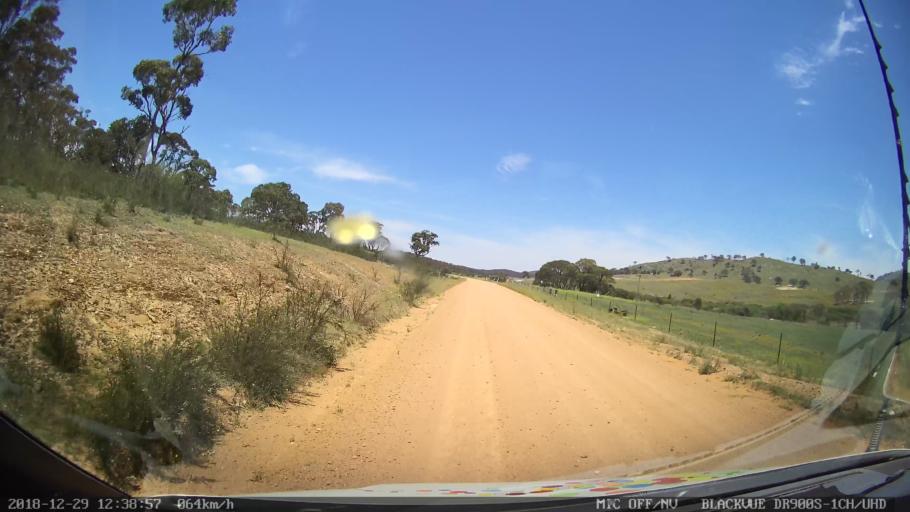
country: AU
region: Australian Capital Territory
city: Macarthur
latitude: -35.5934
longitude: 149.2281
